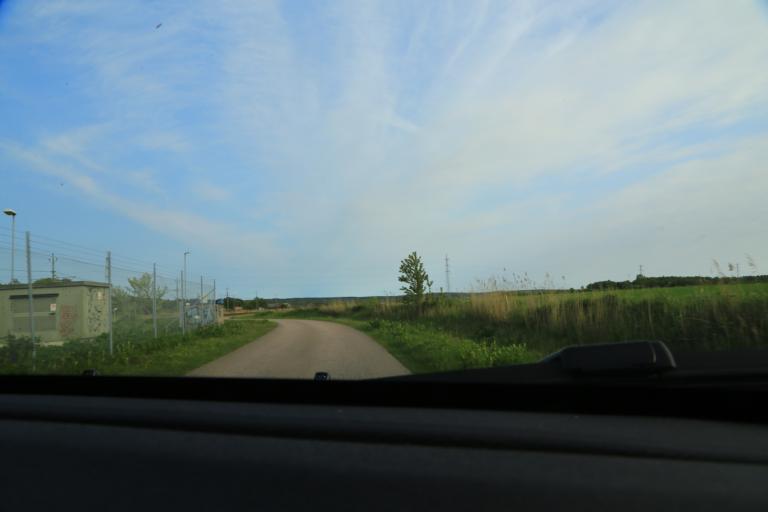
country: SE
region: Halland
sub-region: Kungsbacka Kommun
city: Frillesas
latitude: 57.2386
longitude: 12.1953
